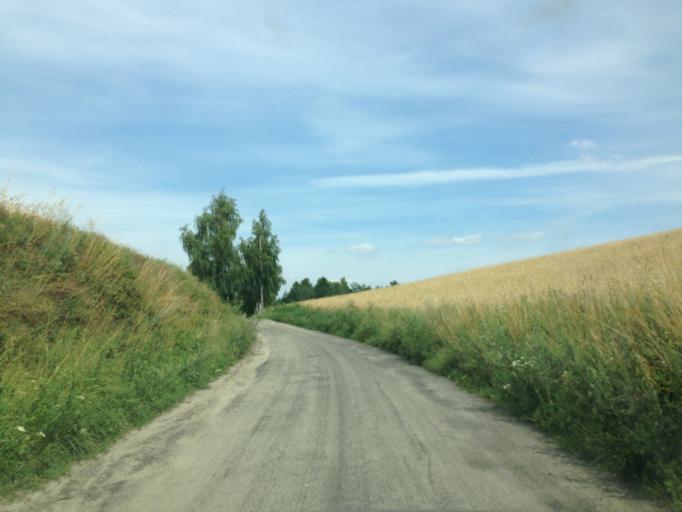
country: PL
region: Kujawsko-Pomorskie
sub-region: Powiat brodnicki
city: Bartniczka
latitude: 53.2533
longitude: 19.5393
